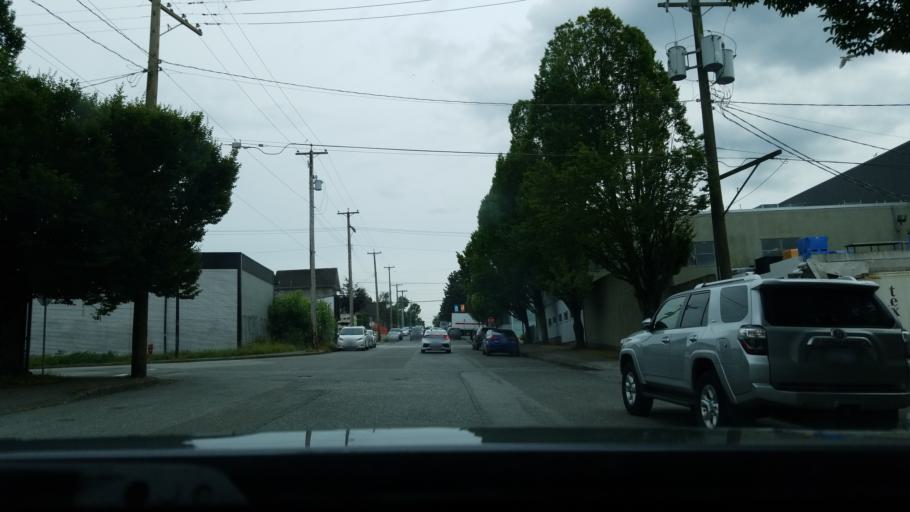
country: CA
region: British Columbia
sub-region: Fraser Valley Regional District
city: North Vancouver
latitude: 49.2838
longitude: -123.0682
